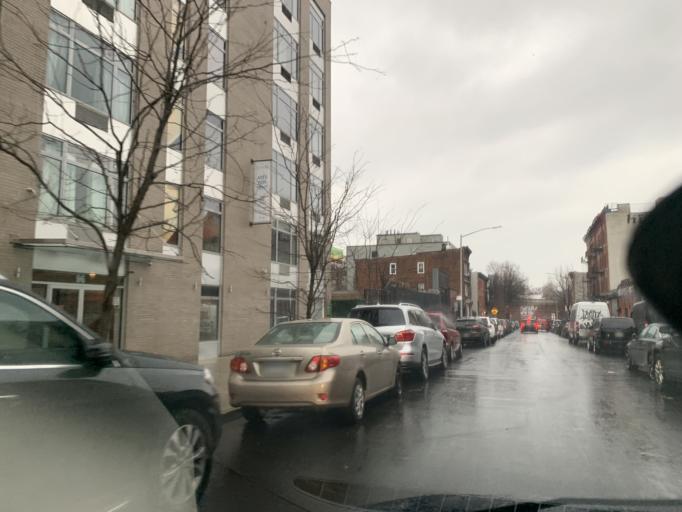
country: US
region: New York
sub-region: Kings County
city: Brooklyn
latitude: 40.6945
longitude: -73.9633
